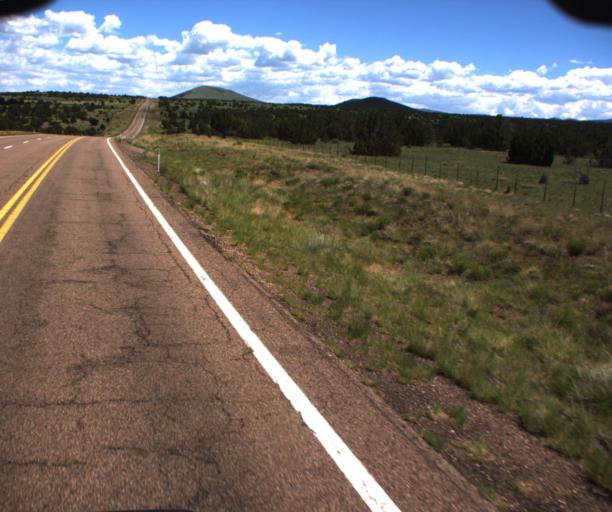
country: US
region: Arizona
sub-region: Apache County
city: Springerville
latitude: 34.2623
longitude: -109.5578
